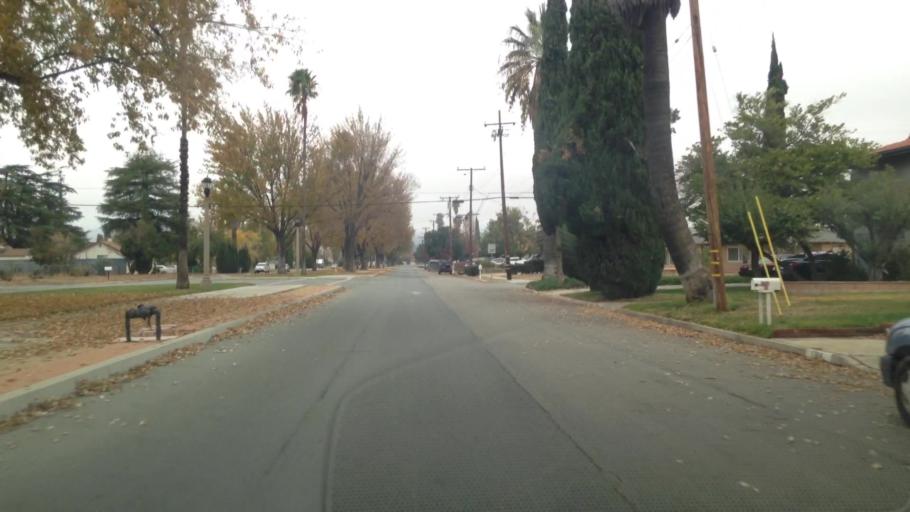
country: US
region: California
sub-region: Riverside County
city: Beaumont
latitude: 33.9429
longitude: -116.9716
